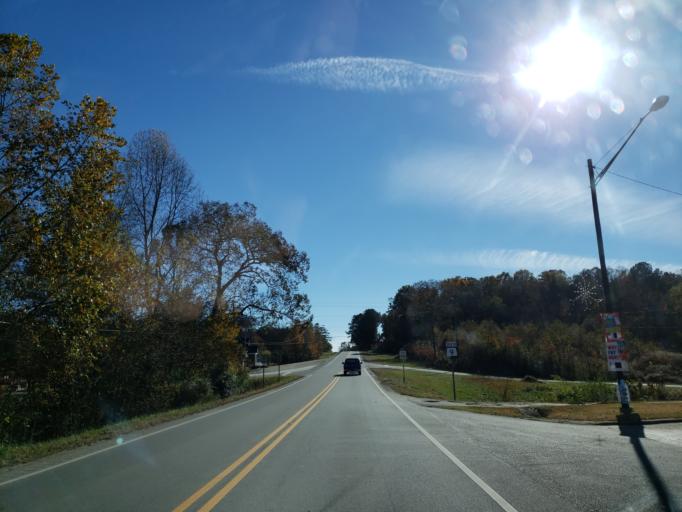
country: US
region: Alabama
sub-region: Cleburne County
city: Heflin
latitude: 33.6195
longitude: -85.5964
